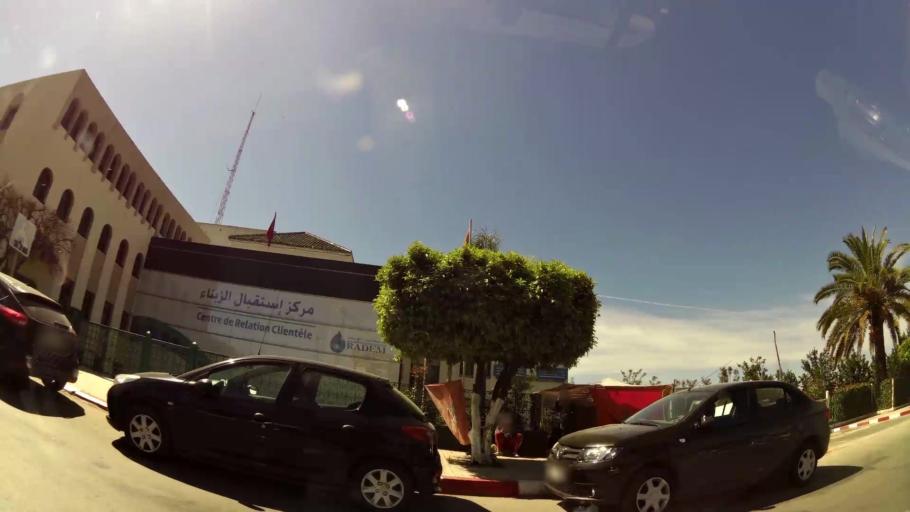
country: MA
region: Meknes-Tafilalet
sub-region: Meknes
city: Meknes
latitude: 33.8940
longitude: -5.5512
